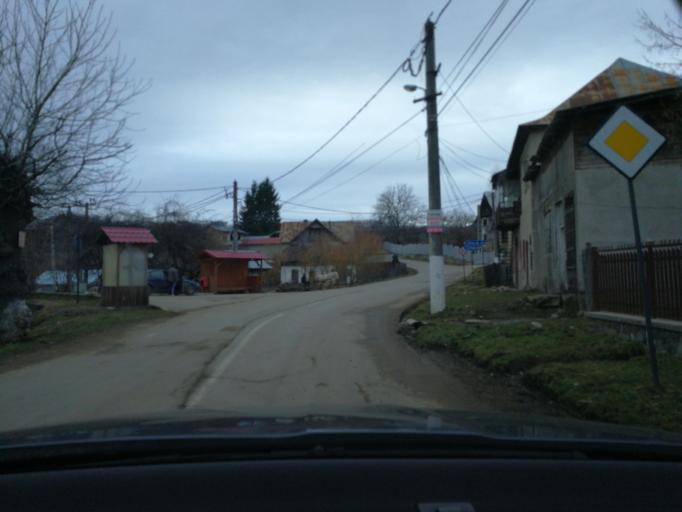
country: RO
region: Prahova
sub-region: Comuna Adunati
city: Ocina de Sus
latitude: 45.1826
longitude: 25.6064
